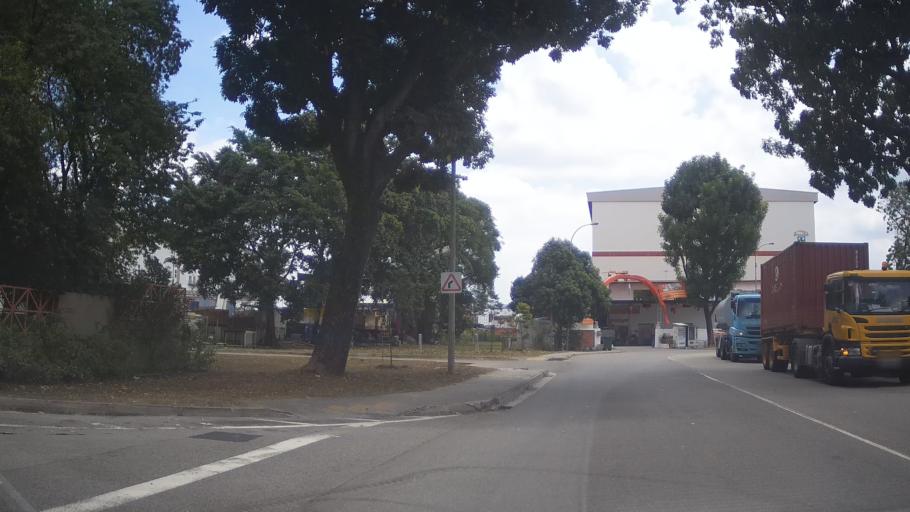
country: SG
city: Singapore
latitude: 1.3111
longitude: 103.7203
